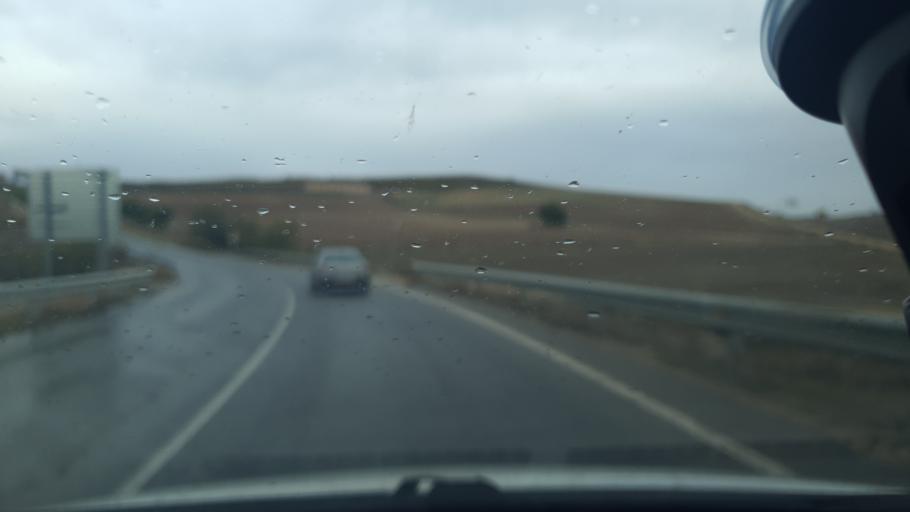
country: ES
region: Castille and Leon
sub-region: Provincia de Segovia
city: Carbonero el Mayor
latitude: 41.1118
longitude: -4.2564
